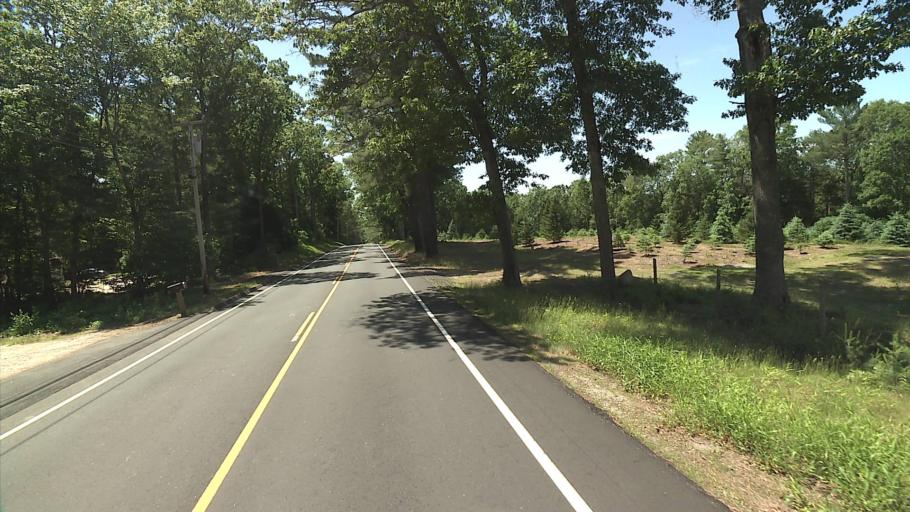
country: US
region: Connecticut
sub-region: Windham County
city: Plainfield
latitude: 41.5932
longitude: -71.8555
